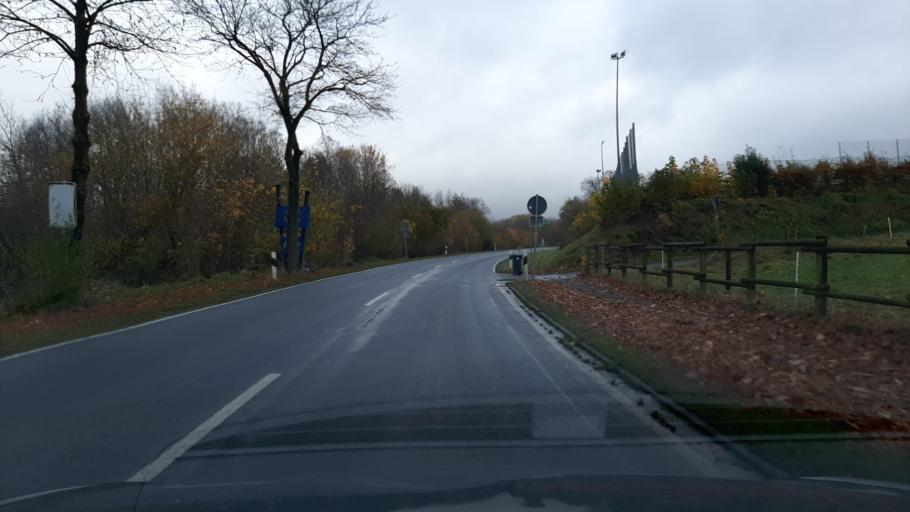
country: DE
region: North Rhine-Westphalia
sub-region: Regierungsbezirk Arnsberg
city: Olsberg
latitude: 51.3243
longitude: 8.5280
